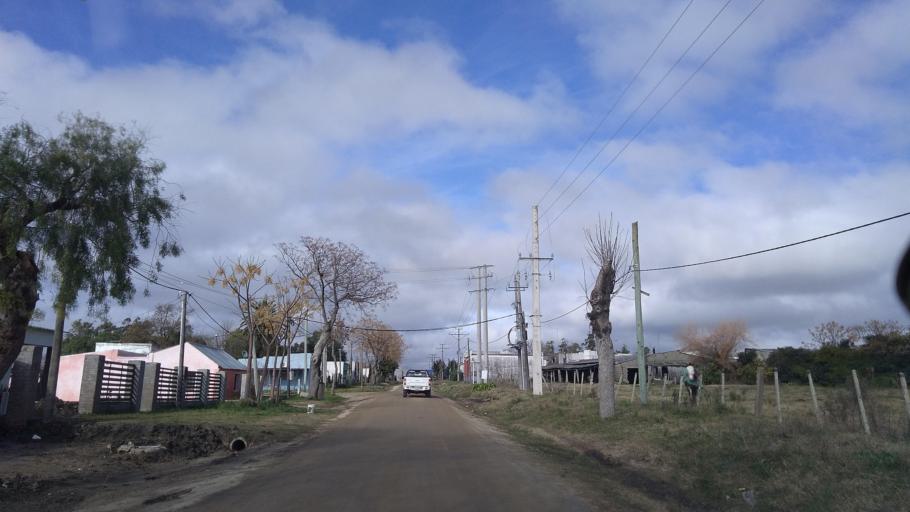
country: UY
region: Canelones
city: Tala
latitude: -34.1935
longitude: -55.7416
